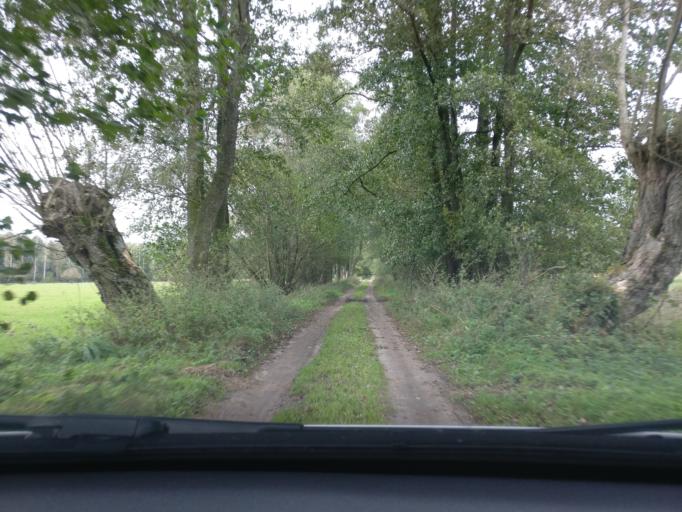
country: PL
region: Masovian Voivodeship
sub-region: Powiat kozienicki
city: Garbatka-Letnisko
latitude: 51.5213
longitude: 21.5999
